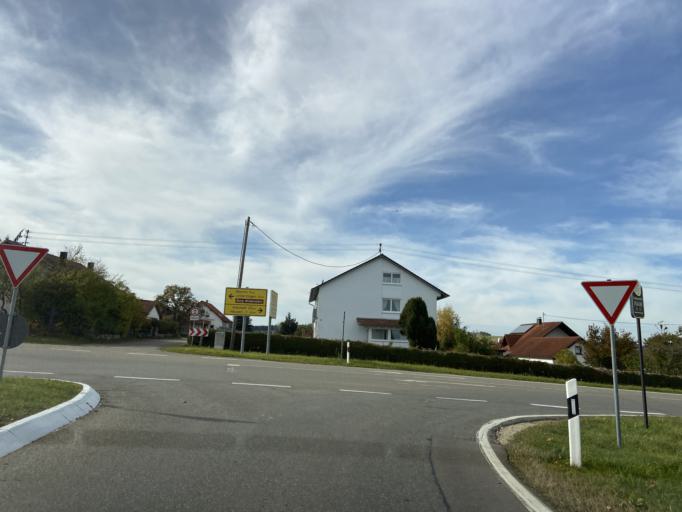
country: DE
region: Baden-Wuerttemberg
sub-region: Tuebingen Region
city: Leibertingen
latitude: 48.0538
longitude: 9.0542
